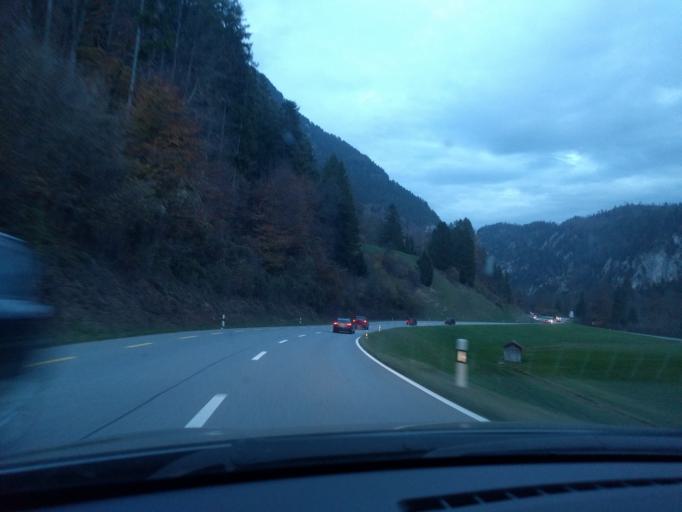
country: CH
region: Bern
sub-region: Frutigen-Niedersimmental District
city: Wimmis
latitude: 46.6692
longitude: 7.6000
